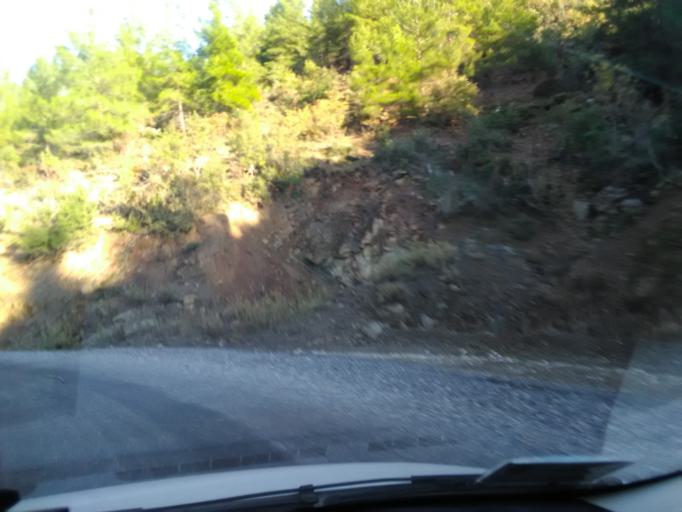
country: TR
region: Antalya
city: Gazipasa
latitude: 36.3050
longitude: 32.4023
